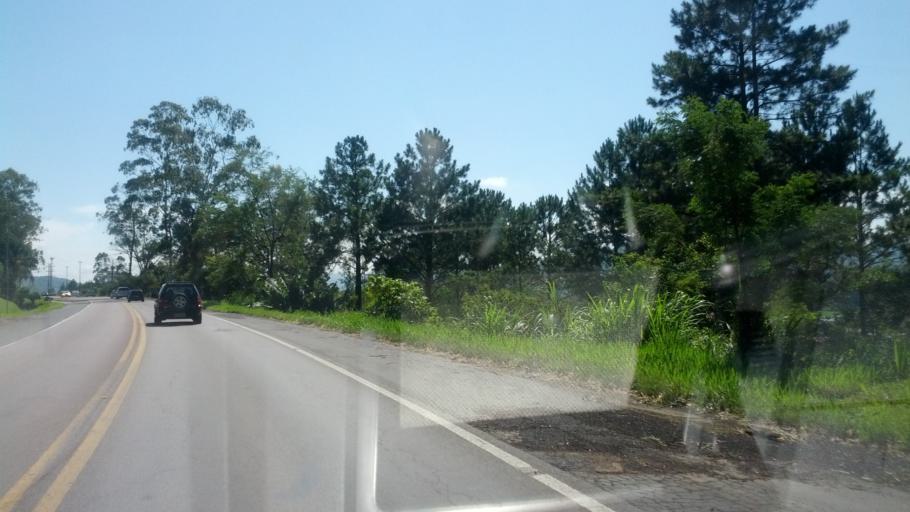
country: BR
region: Santa Catarina
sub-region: Rio Do Sul
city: Rio do Sul
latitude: -27.1880
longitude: -49.6097
